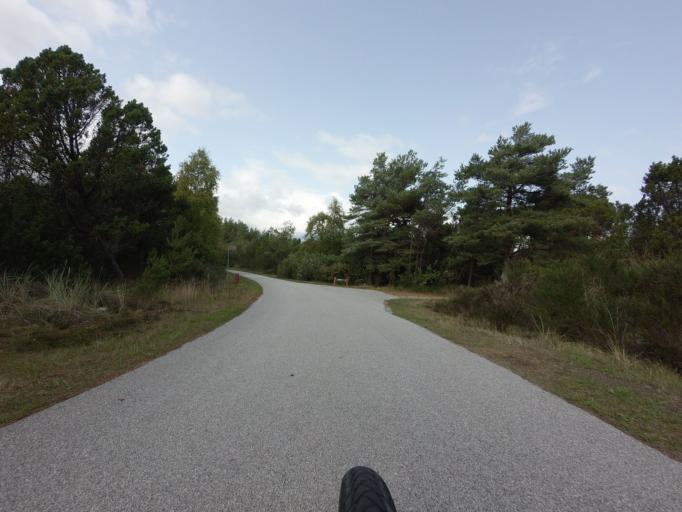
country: DK
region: North Denmark
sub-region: Frederikshavn Kommune
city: Strandby
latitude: 57.6430
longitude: 10.4369
